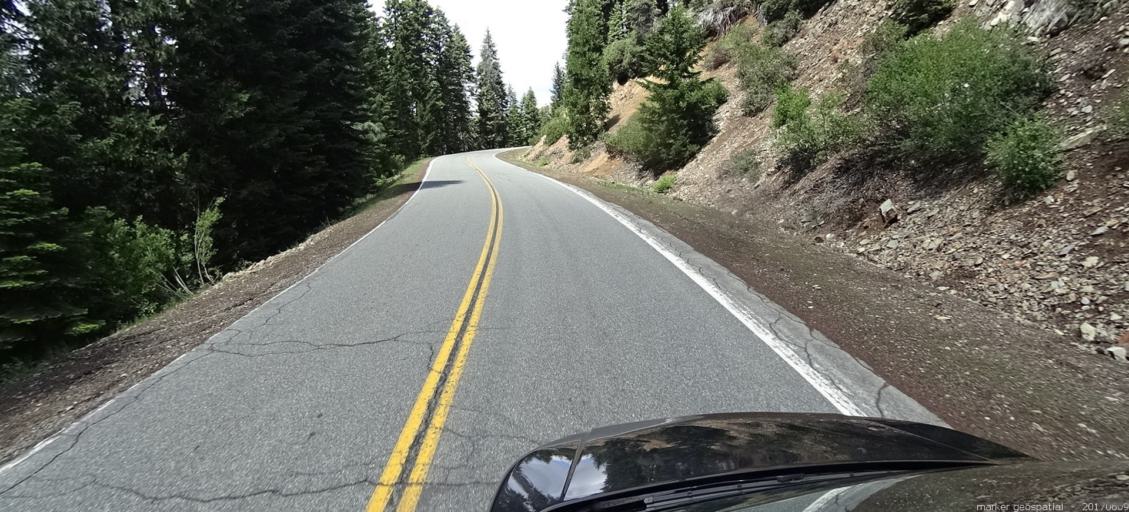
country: US
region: California
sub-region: Siskiyou County
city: Yreka
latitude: 41.3849
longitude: -122.9959
